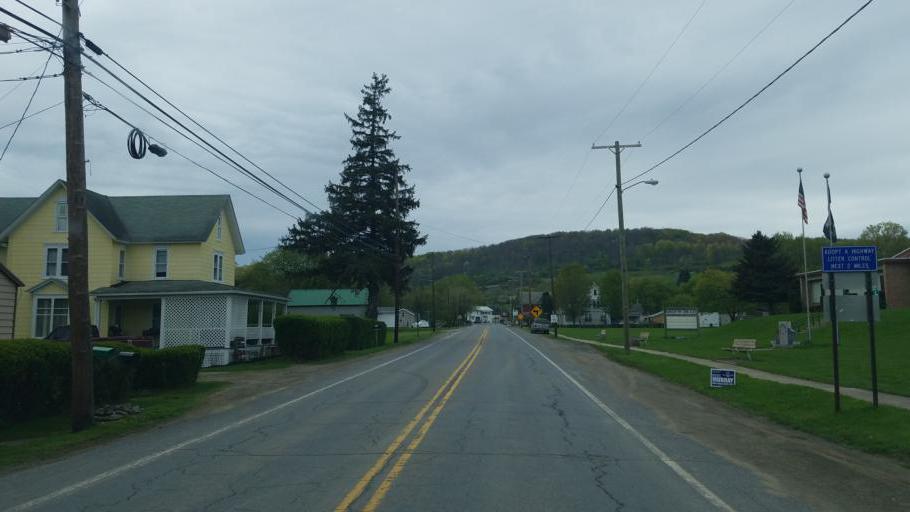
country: US
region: Pennsylvania
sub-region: Tioga County
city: Westfield
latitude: 41.9400
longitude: -77.6471
